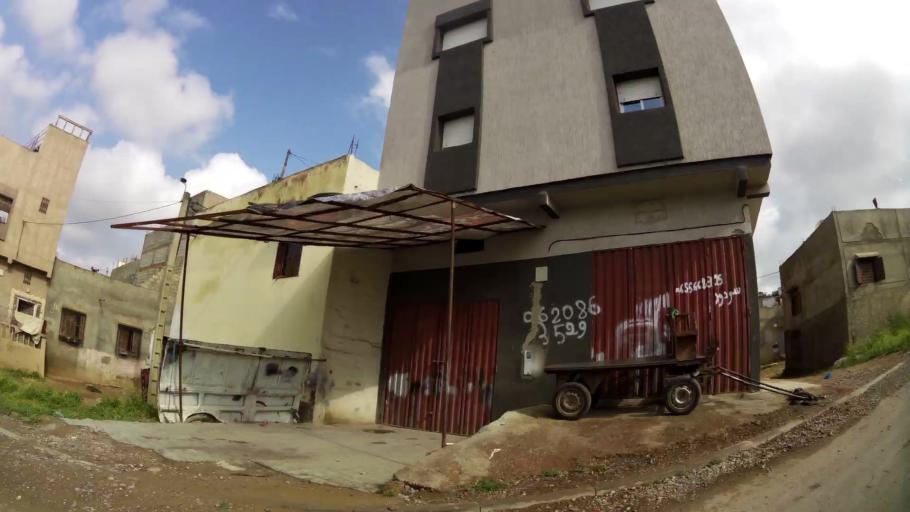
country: MA
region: Rabat-Sale-Zemmour-Zaer
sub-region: Khemisset
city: Tiflet
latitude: 33.8886
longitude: -6.3064
